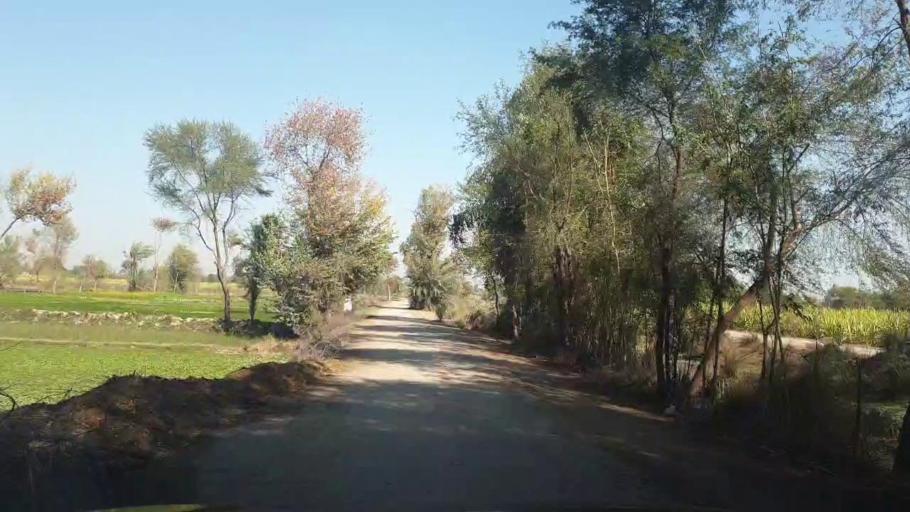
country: PK
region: Sindh
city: Ghotki
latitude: 27.9828
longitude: 69.4257
